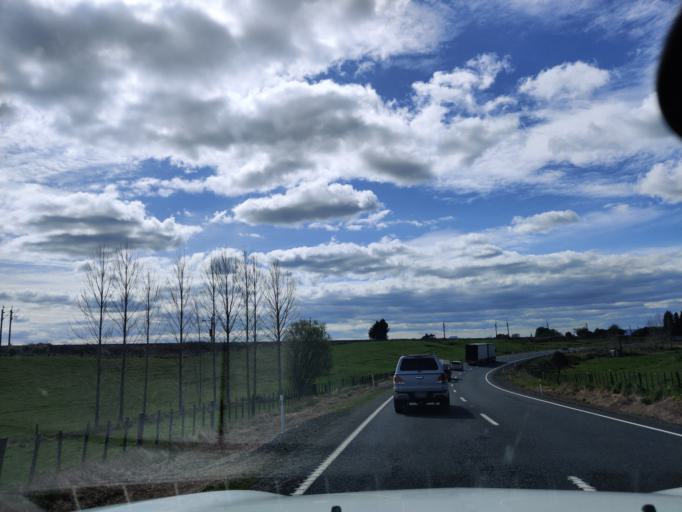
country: NZ
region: Waikato
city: Turangi
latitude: -39.0330
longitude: 175.3818
